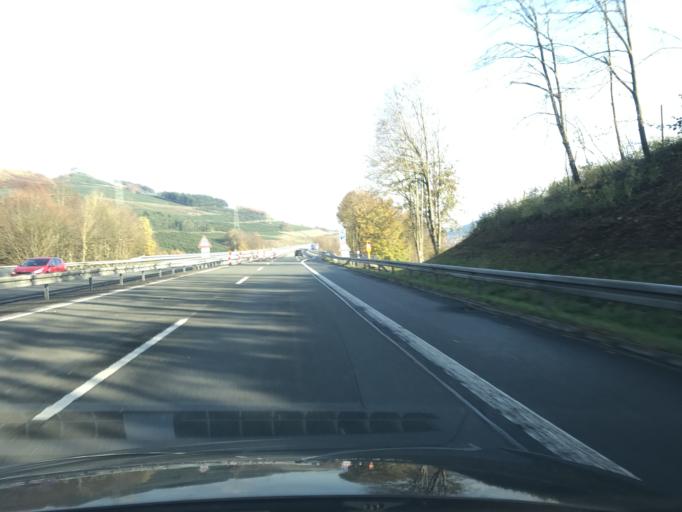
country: DE
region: North Rhine-Westphalia
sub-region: Regierungsbezirk Arnsberg
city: Bestwig
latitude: 51.3601
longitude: 8.3573
